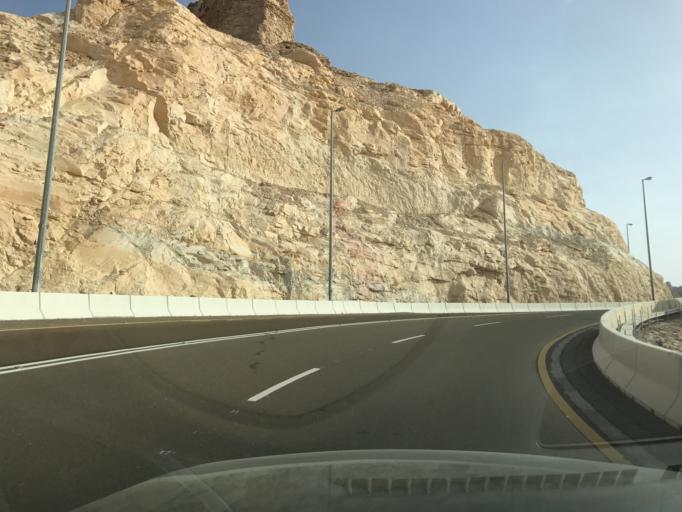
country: AE
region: Abu Dhabi
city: Al Ain
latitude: 24.1009
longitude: 55.7593
